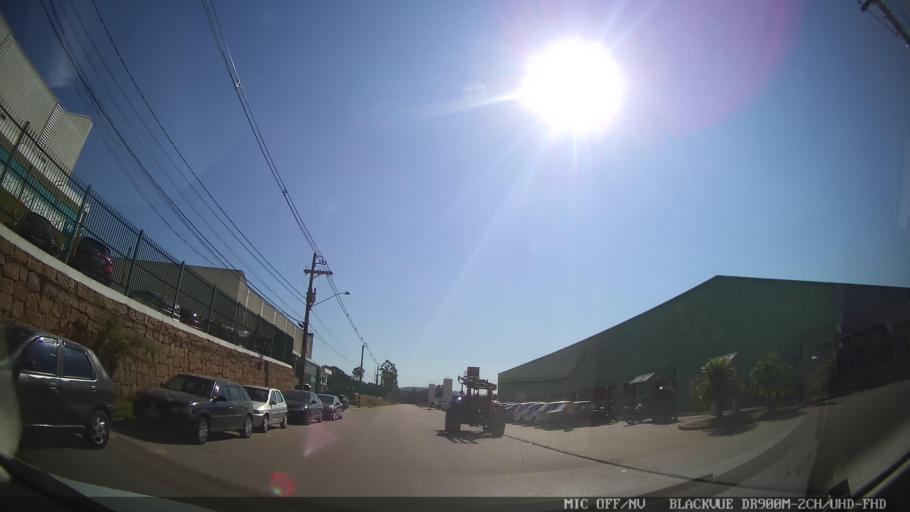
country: BR
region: Sao Paulo
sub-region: Itupeva
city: Itupeva
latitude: -23.1335
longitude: -47.0444
